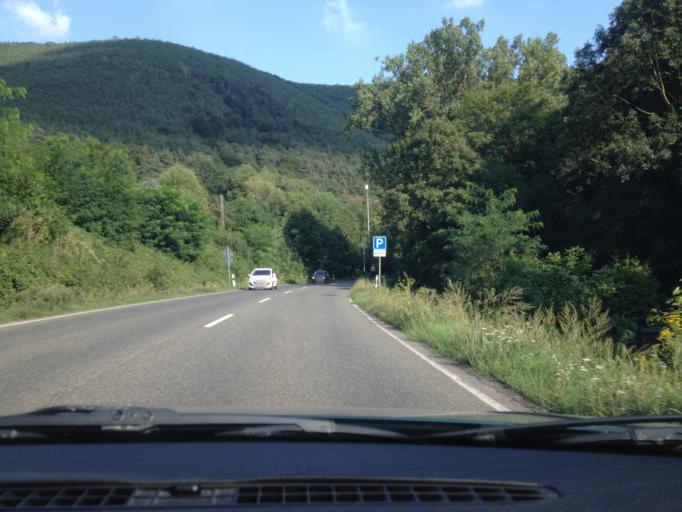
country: DE
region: Rheinland-Pfalz
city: Lindenberg
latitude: 49.3682
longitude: 8.1037
